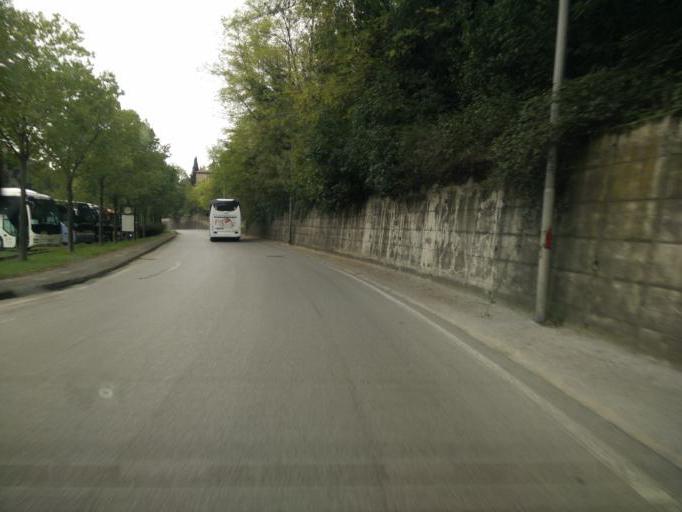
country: IT
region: Tuscany
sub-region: Provincia di Siena
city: Siena
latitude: 43.3162
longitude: 11.3162
